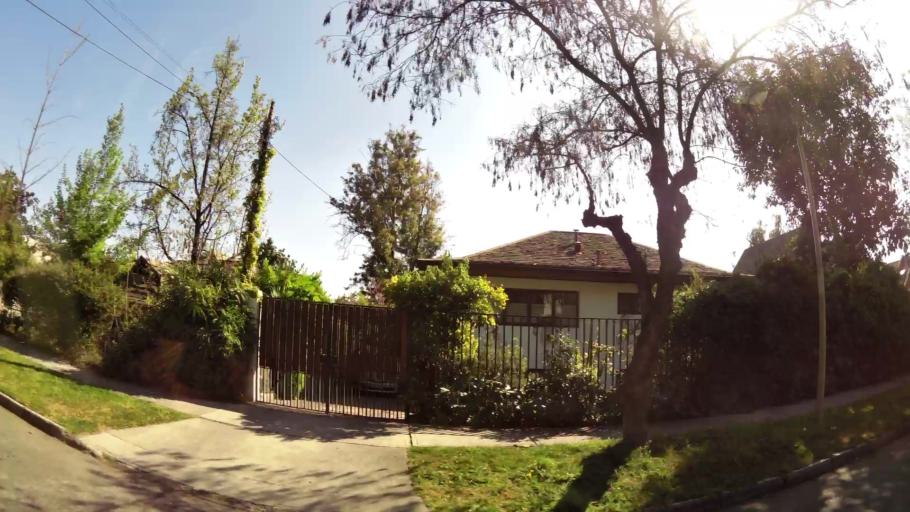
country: CL
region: Santiago Metropolitan
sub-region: Provincia de Santiago
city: Villa Presidente Frei, Nunoa, Santiago, Chile
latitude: -33.4026
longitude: -70.5409
